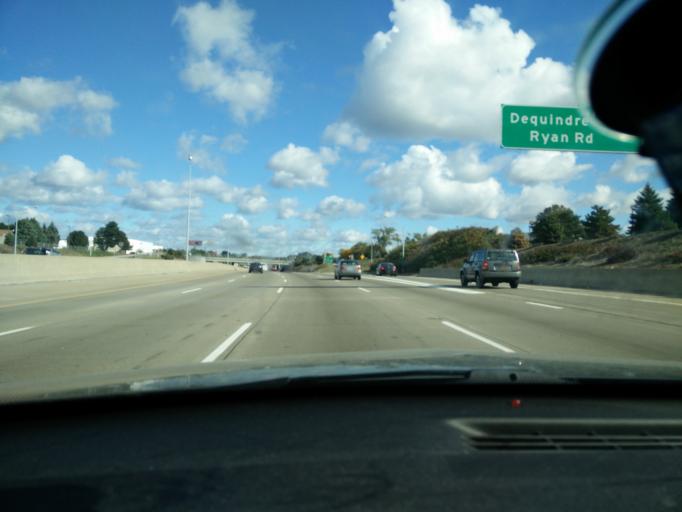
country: US
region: Michigan
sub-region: Oakland County
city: Madison Heights
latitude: 42.4793
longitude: -83.0881
